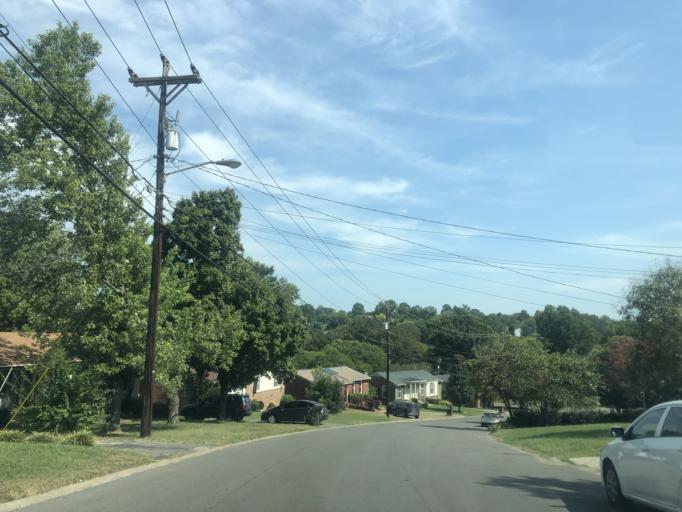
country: US
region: Tennessee
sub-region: Williamson County
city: Brentwood Estates
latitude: 36.0506
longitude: -86.7064
